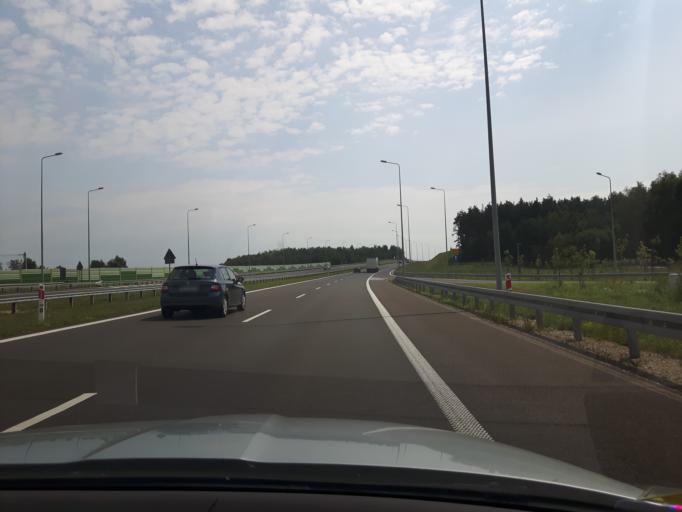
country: PL
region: Warmian-Masurian Voivodeship
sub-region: Powiat nidzicki
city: Nidzica
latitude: 53.3722
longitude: 20.3840
